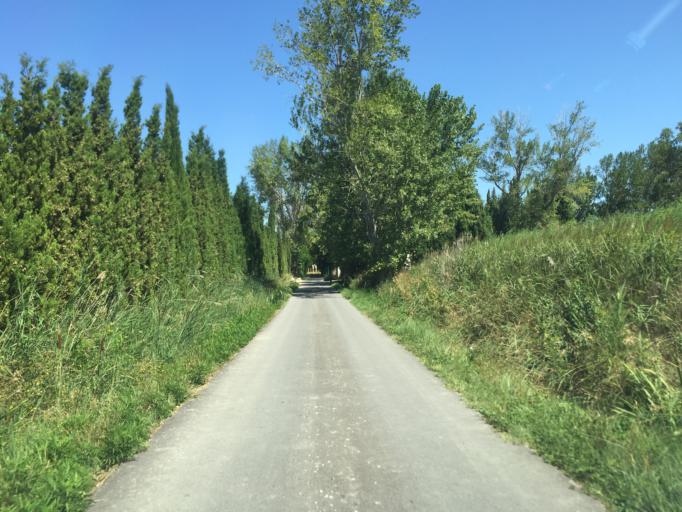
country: FR
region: Provence-Alpes-Cote d'Azur
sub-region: Departement du Vaucluse
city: Orange
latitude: 44.1246
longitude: 4.8461
